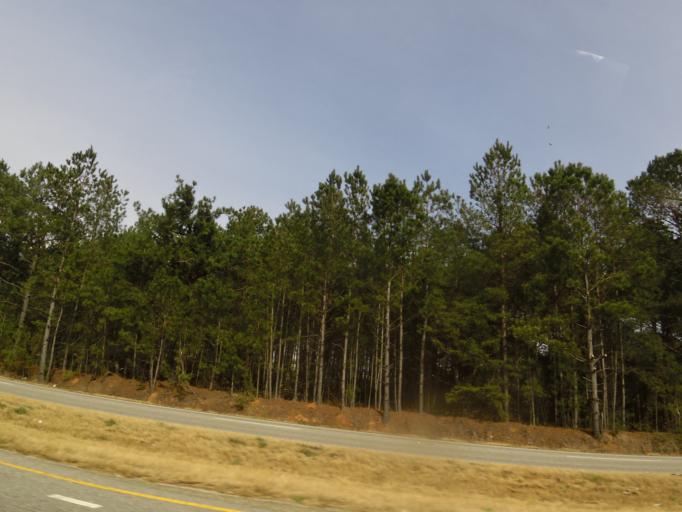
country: US
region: Alabama
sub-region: Dale County
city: Midland City
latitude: 31.3277
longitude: -85.5291
